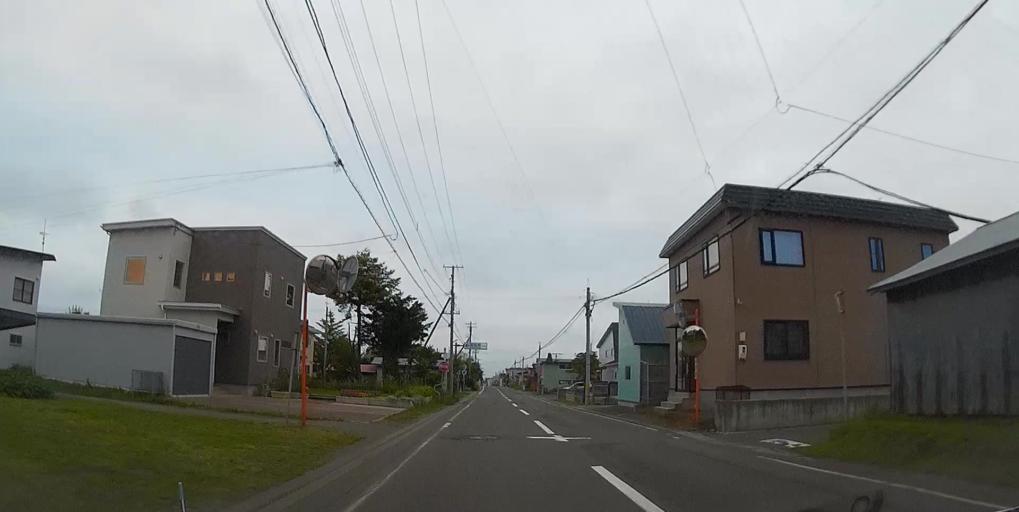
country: JP
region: Hokkaido
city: Nanae
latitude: 42.2542
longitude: 140.2578
